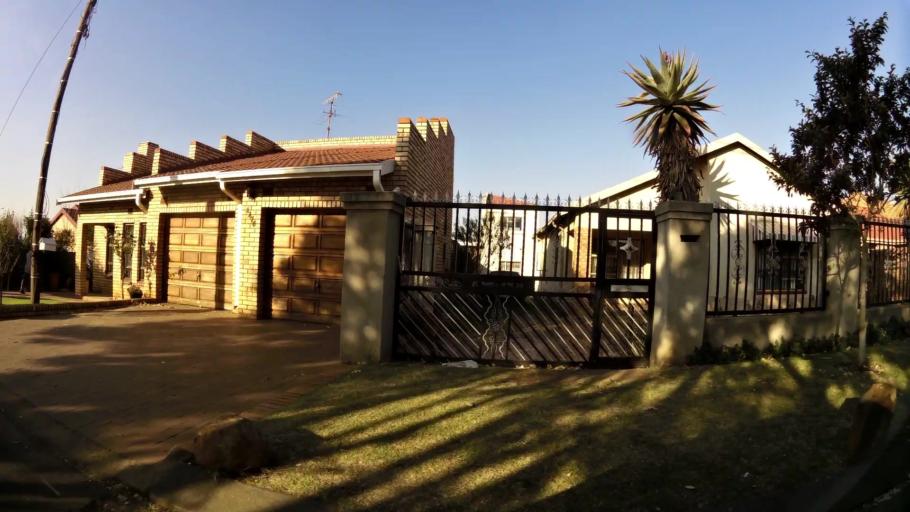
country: ZA
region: Gauteng
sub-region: City of Johannesburg Metropolitan Municipality
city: Soweto
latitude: -26.2652
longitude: 27.8752
